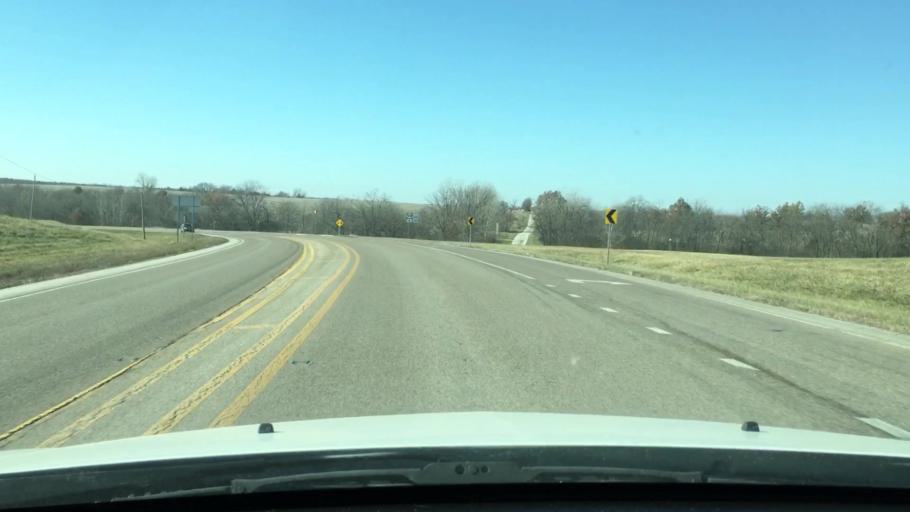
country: US
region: Illinois
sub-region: Pike County
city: Pittsfield
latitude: 39.6051
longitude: -90.8730
